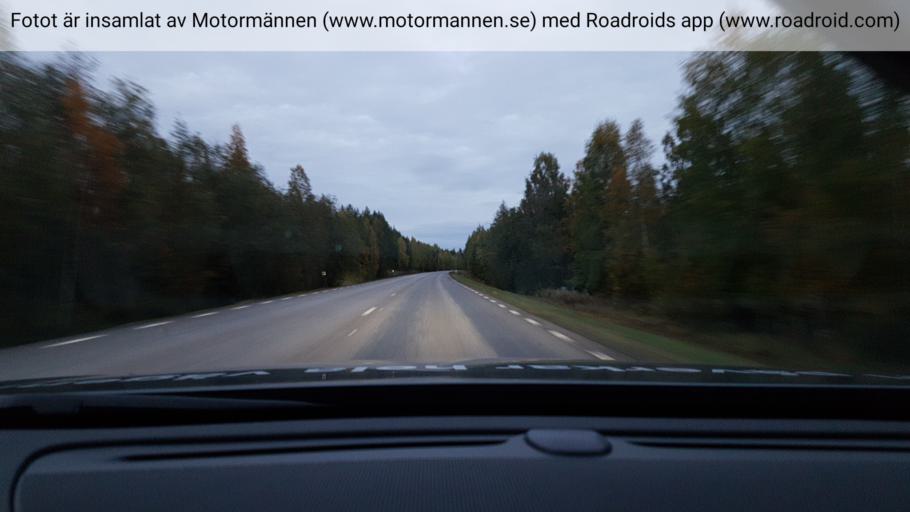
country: SE
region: Norrbotten
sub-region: Alvsbyns Kommun
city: AElvsbyn
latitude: 65.7810
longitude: 20.8177
